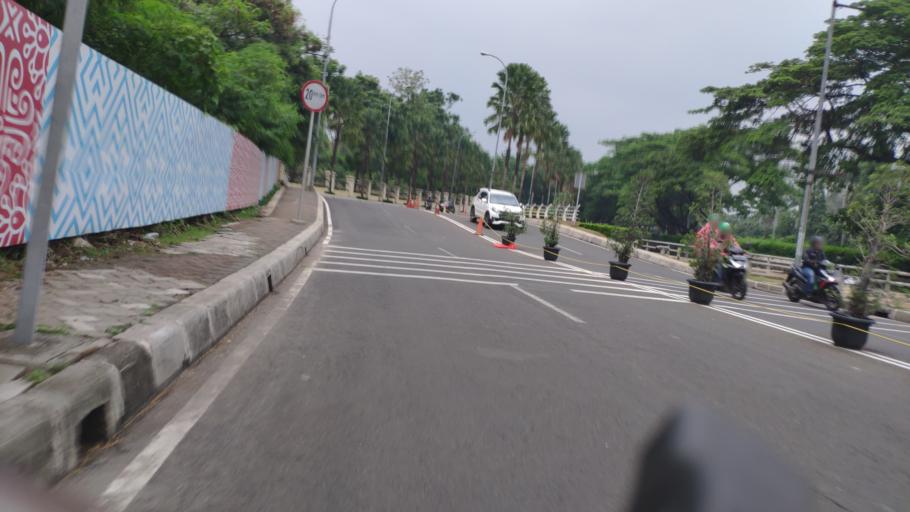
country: ID
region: Jakarta Raya
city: Jakarta
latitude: -6.2198
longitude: 106.8355
